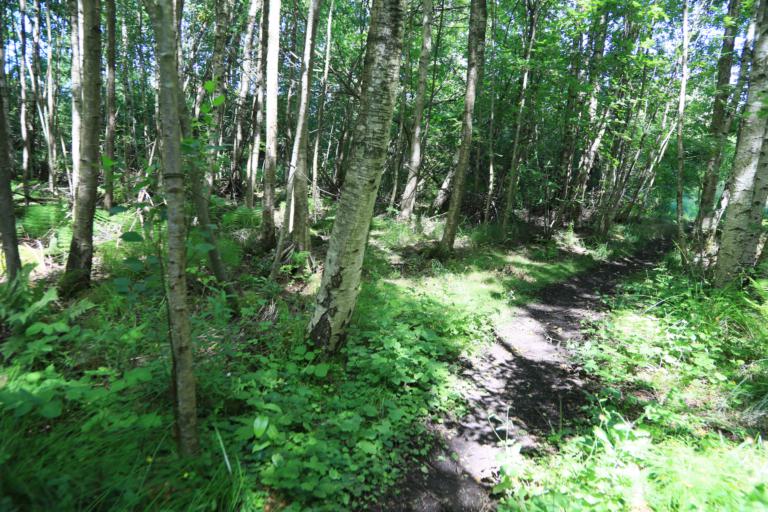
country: SE
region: Halland
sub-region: Varbergs Kommun
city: Traslovslage
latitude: 57.0984
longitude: 12.2862
